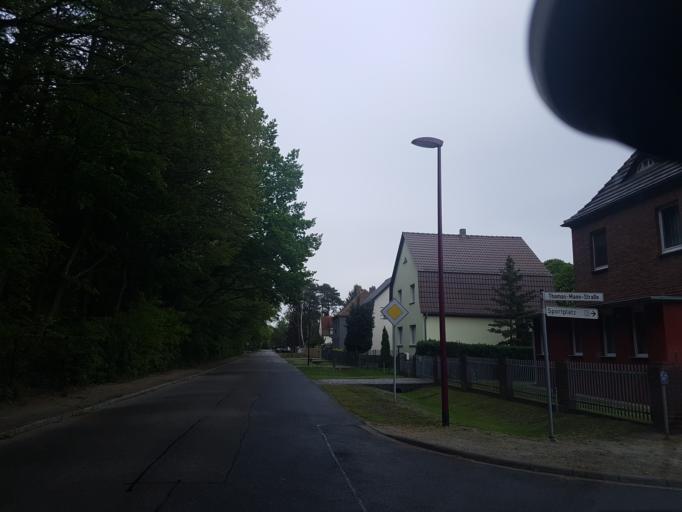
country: DE
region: Brandenburg
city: Neupetershain
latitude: 51.6065
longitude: 14.1676
